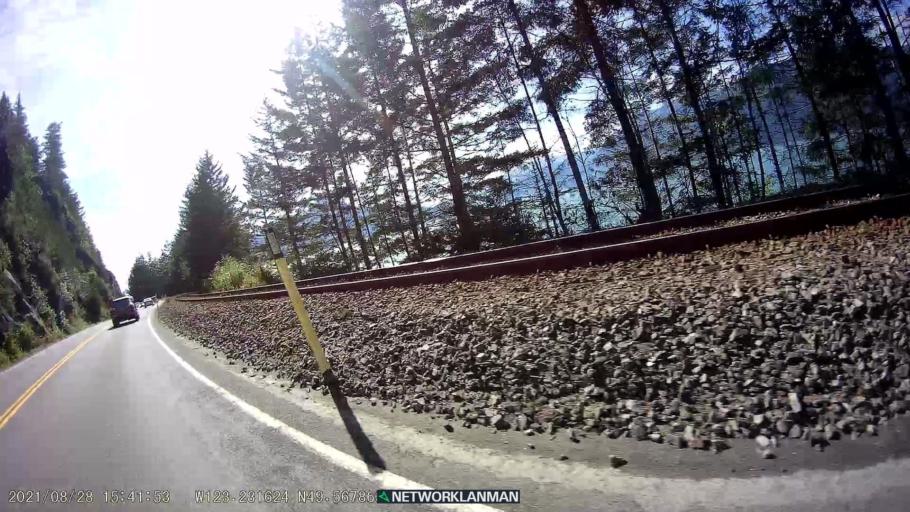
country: CA
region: British Columbia
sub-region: Greater Vancouver Regional District
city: Lions Bay
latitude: 49.5677
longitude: -123.2314
